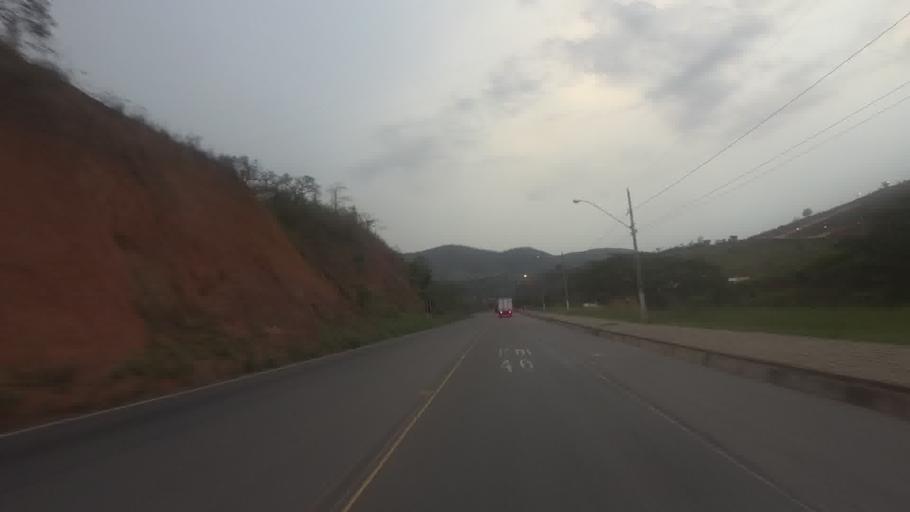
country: BR
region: Minas Gerais
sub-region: Alem Paraiba
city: Alem Paraiba
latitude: -21.8668
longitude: -42.6711
